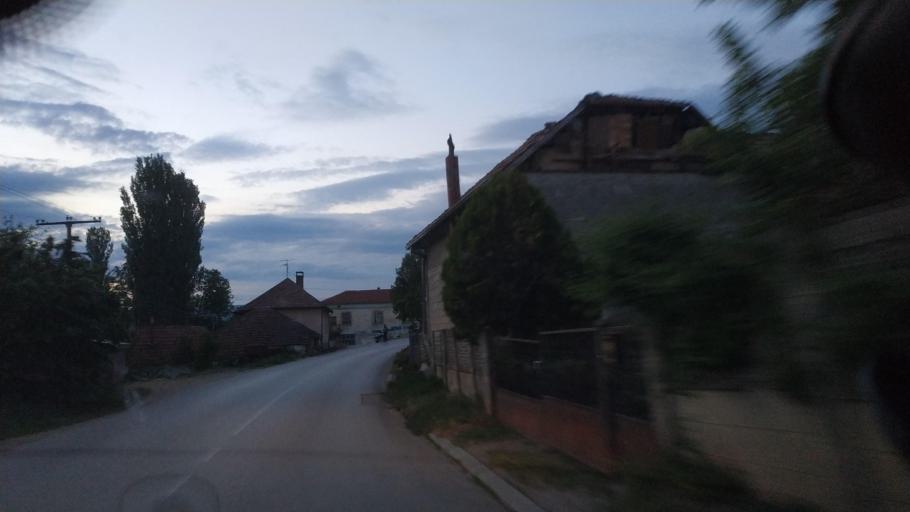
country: RS
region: Central Serbia
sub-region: Nisavski Okrug
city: Merosina
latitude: 43.2957
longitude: 21.7046
